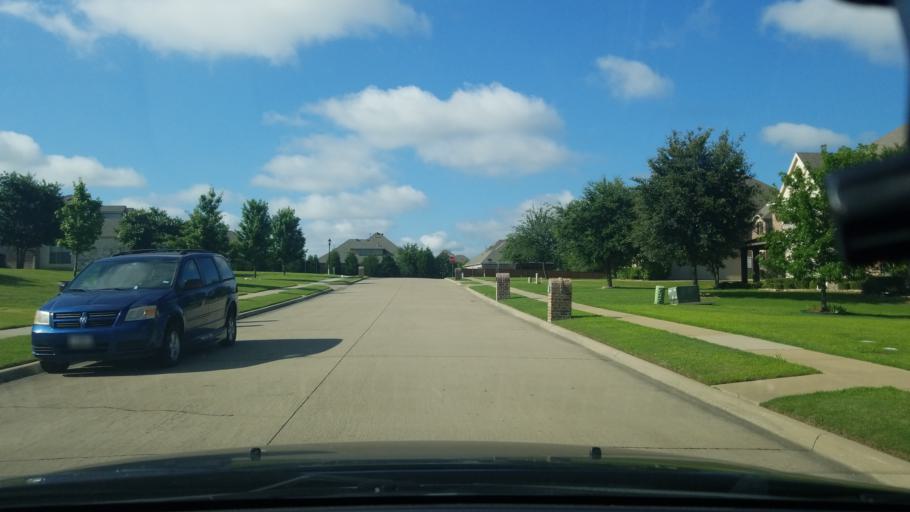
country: US
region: Texas
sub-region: Dallas County
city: Sunnyvale
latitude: 32.8079
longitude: -96.5631
